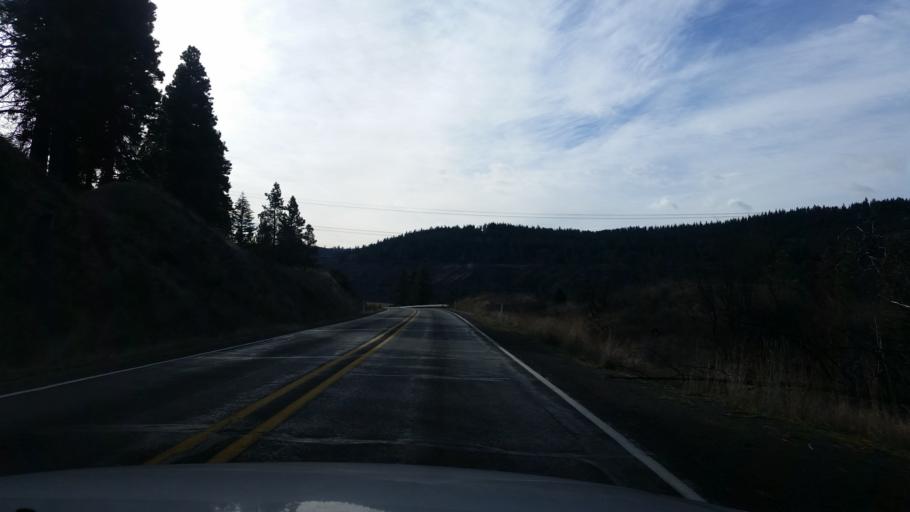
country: US
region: Washington
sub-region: Kittitas County
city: Cle Elum
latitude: 47.1581
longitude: -120.8072
